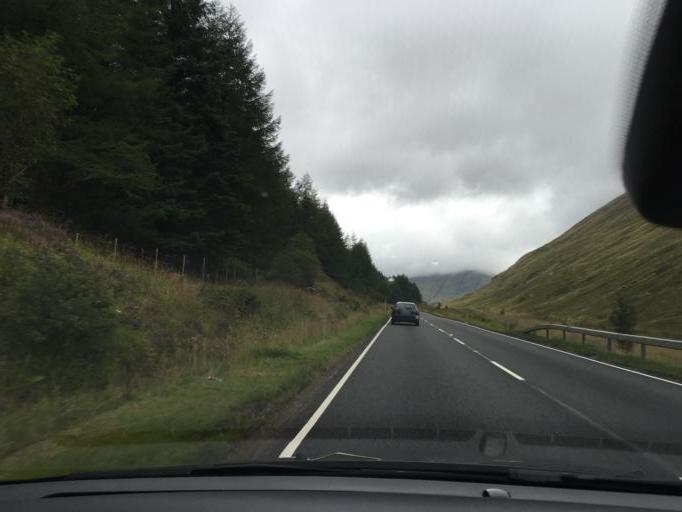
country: GB
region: Scotland
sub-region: Argyll and Bute
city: Garelochhead
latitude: 56.4498
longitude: -4.7099
